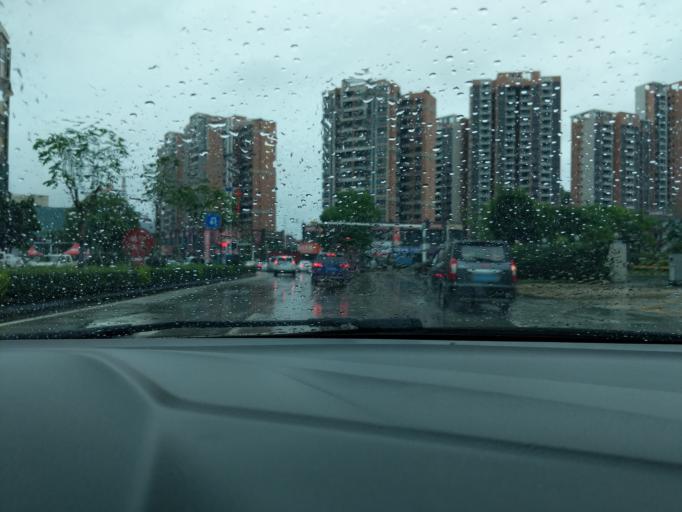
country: CN
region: Guangdong
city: Pingshi
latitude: 22.2018
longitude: 112.3295
